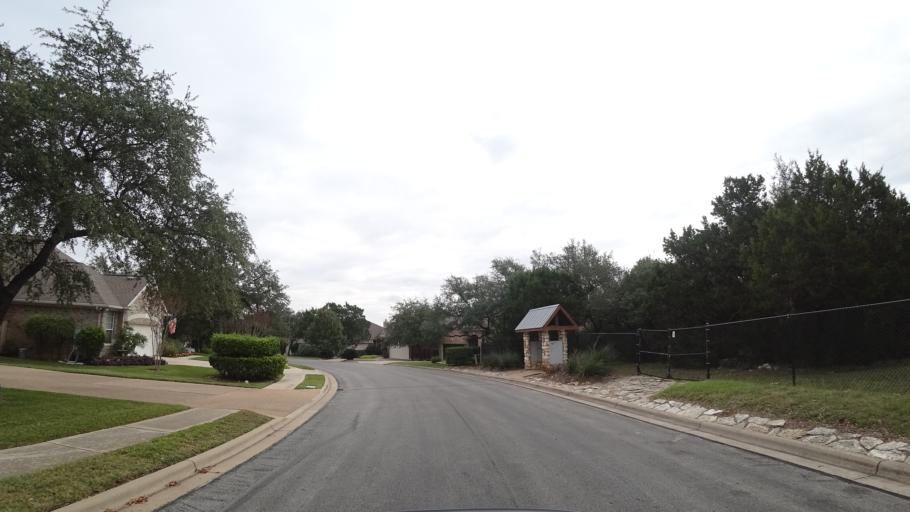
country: US
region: Texas
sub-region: Travis County
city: Shady Hollow
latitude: 30.1949
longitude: -97.8998
